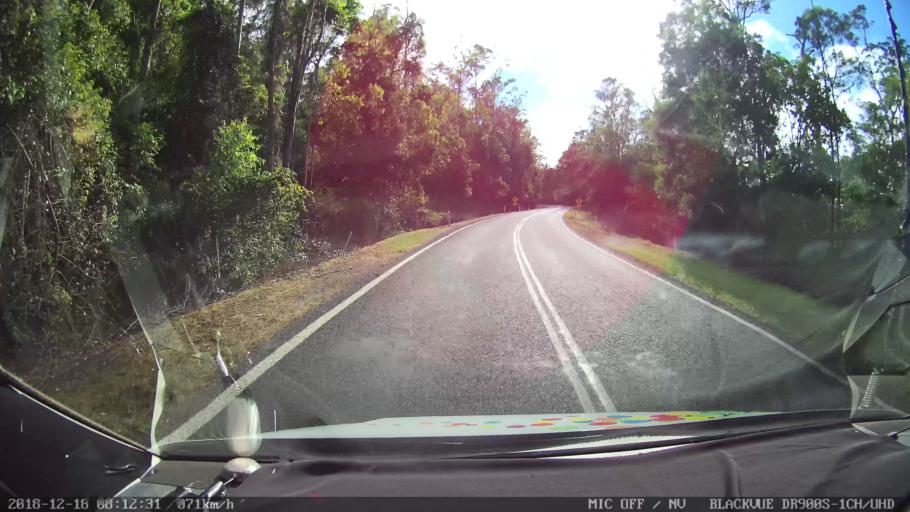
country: AU
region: New South Wales
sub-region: Kyogle
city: Kyogle
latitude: -28.3391
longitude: 152.6715
